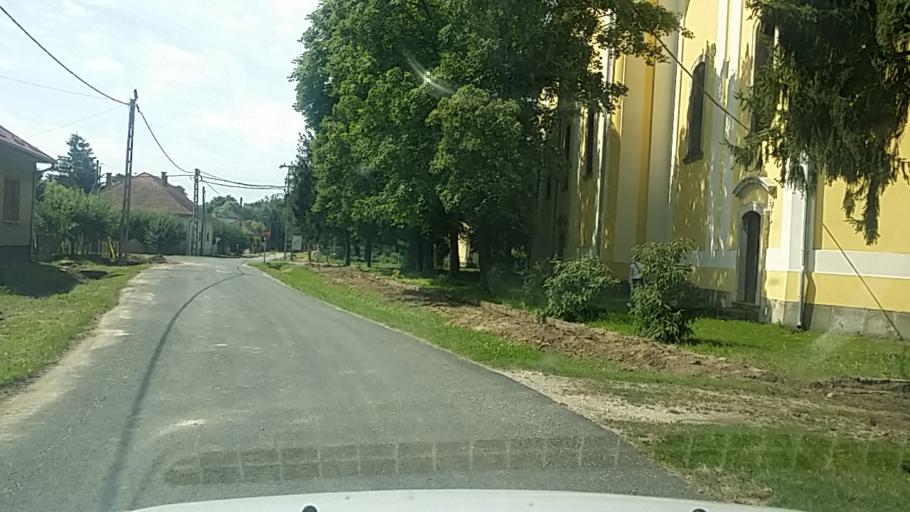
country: HU
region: Zala
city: Lenti
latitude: 46.5735
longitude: 16.5934
